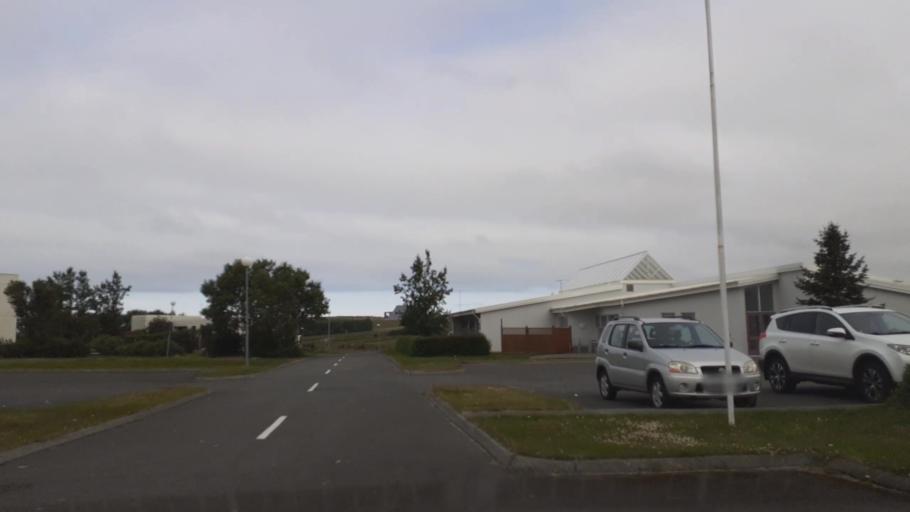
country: IS
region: Northwest
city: Saudarkrokur
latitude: 65.6557
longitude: -20.2779
